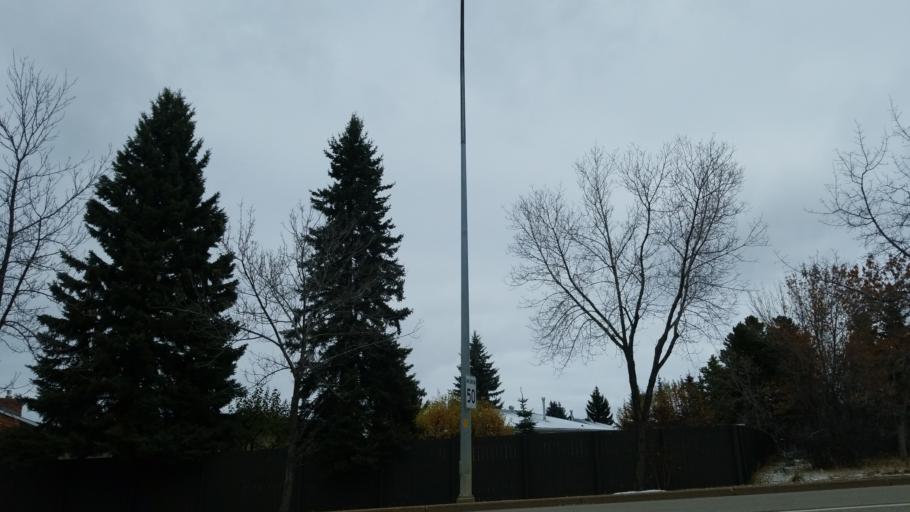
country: CA
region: Alberta
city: Sherwood Park
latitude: 53.5283
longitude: -113.2809
